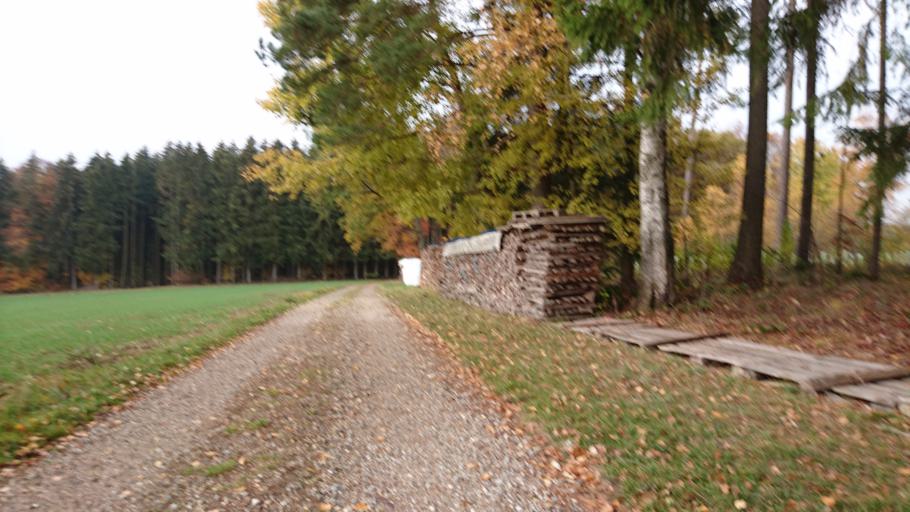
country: DE
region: Bavaria
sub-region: Swabia
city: Zusmarshausen
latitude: 48.4351
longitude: 10.6173
